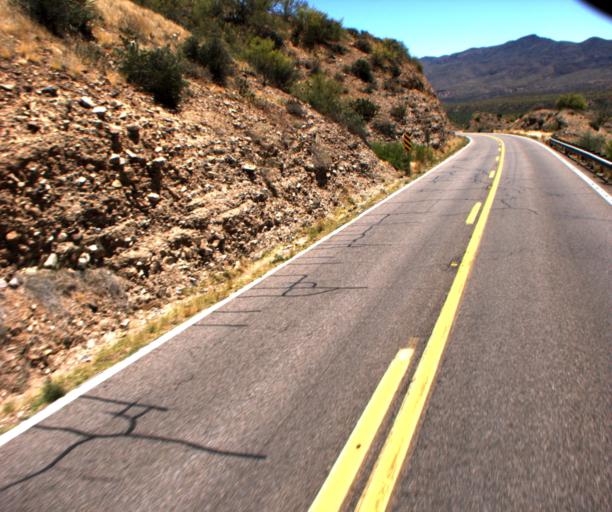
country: US
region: Arizona
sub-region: Pinal County
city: Kearny
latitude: 33.1629
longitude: -110.8050
